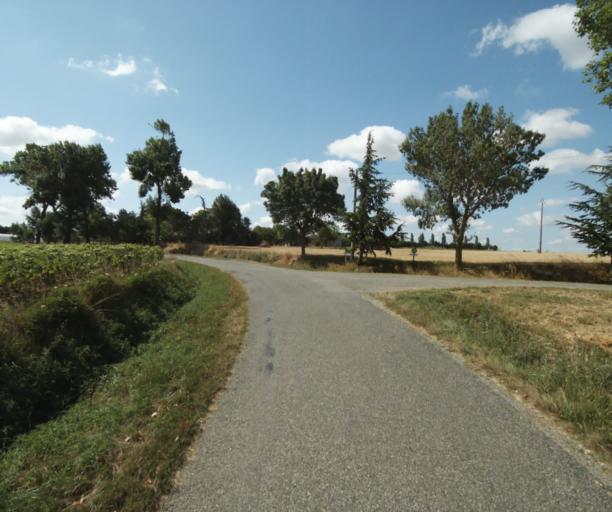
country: FR
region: Midi-Pyrenees
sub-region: Departement de la Haute-Garonne
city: Auriac-sur-Vendinelle
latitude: 43.4529
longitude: 1.7893
